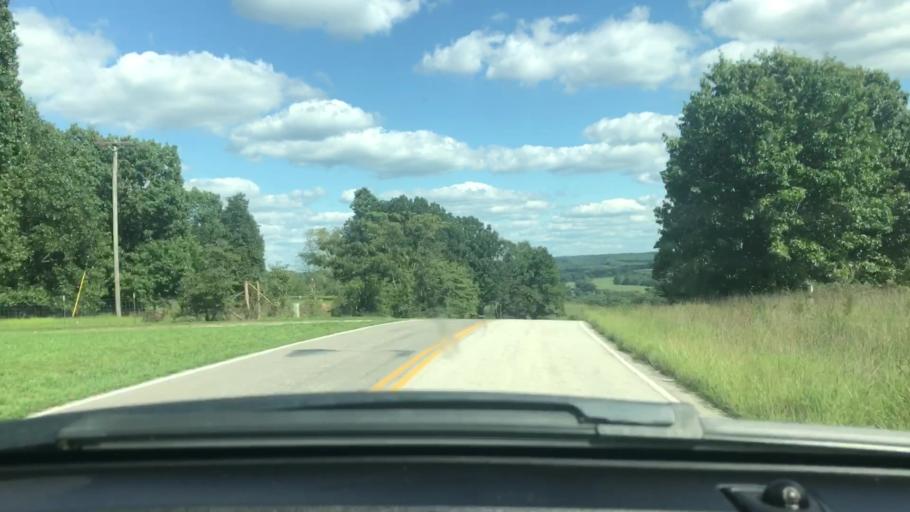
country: US
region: Missouri
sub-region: Wright County
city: Hartville
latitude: 37.3767
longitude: -92.4081
